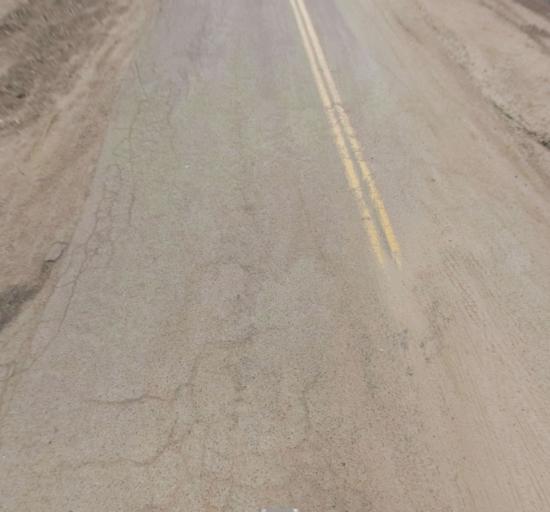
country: US
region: California
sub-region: Madera County
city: Chowchilla
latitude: 37.0690
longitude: -120.4371
